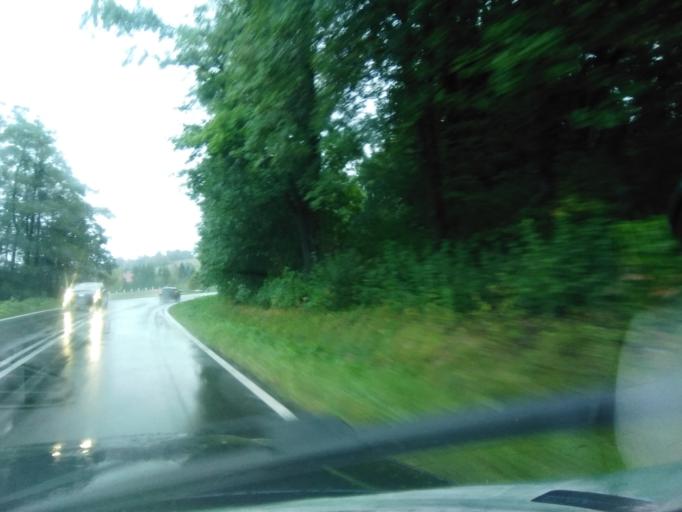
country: PL
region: Subcarpathian Voivodeship
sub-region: Powiat ropczycko-sedziszowski
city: Niedzwiada
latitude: 49.9894
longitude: 21.5622
